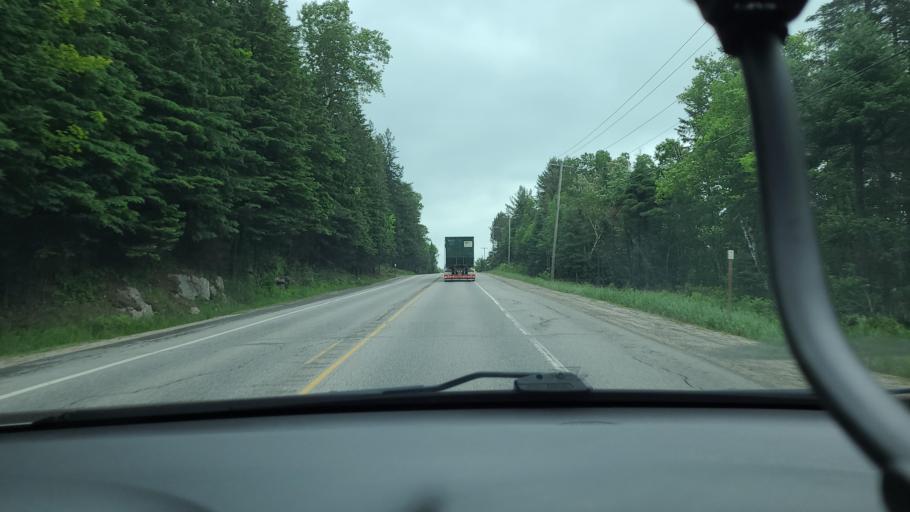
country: CA
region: Quebec
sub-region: Laurentides
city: Labelle
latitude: 46.3163
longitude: -74.7893
